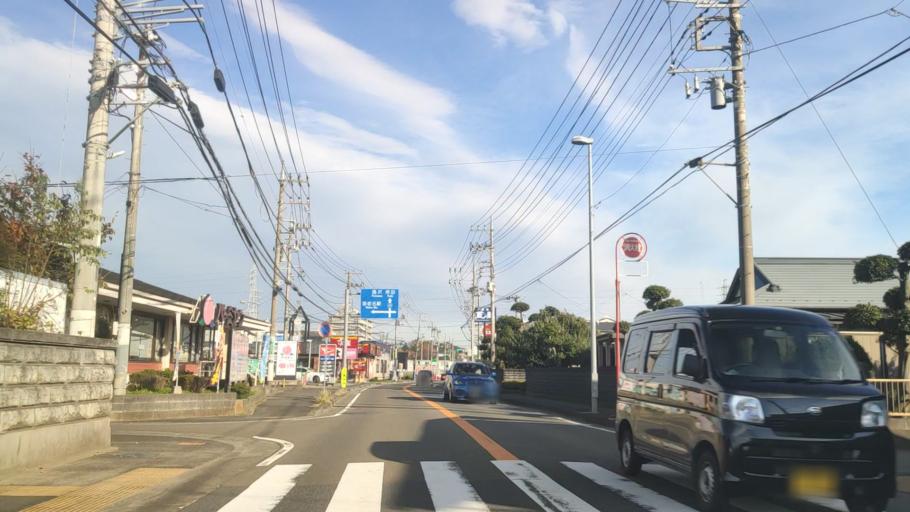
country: JP
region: Kanagawa
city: Atsugi
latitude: 35.4214
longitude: 139.3900
